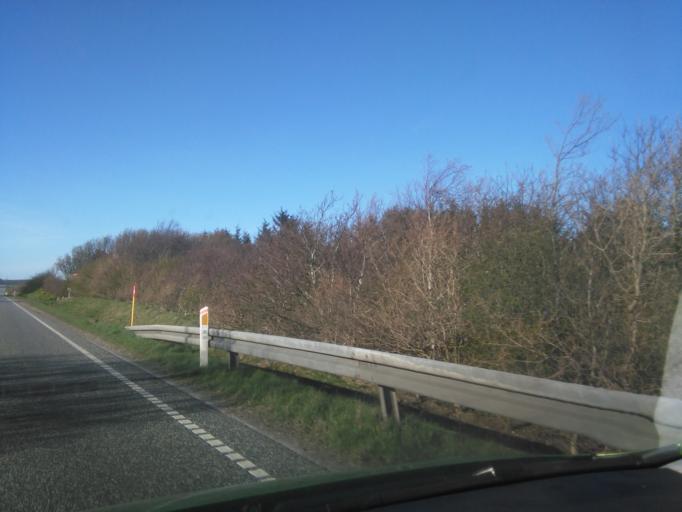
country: DK
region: Central Jutland
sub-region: Ringkobing-Skjern Kommune
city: Skjern
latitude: 56.0609
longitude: 8.5045
